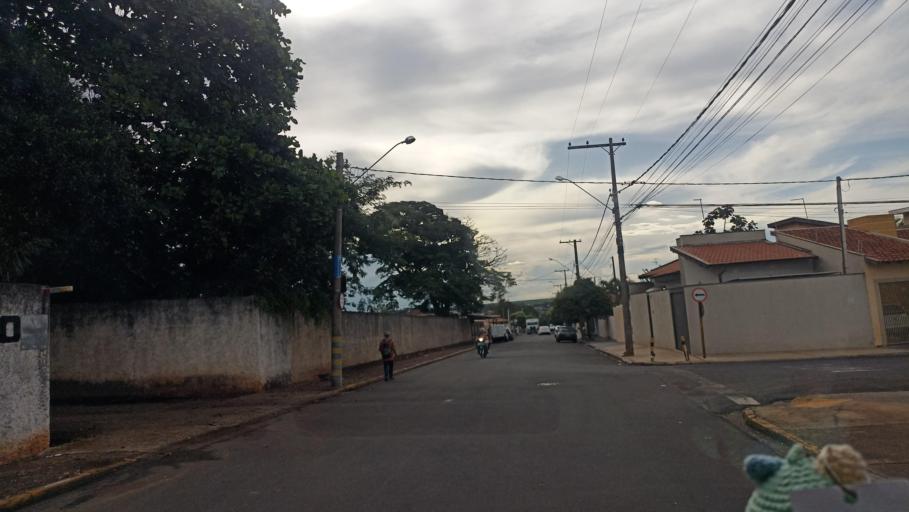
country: BR
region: Sao Paulo
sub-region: Jaboticabal
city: Jaboticabal
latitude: -21.2590
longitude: -48.3277
